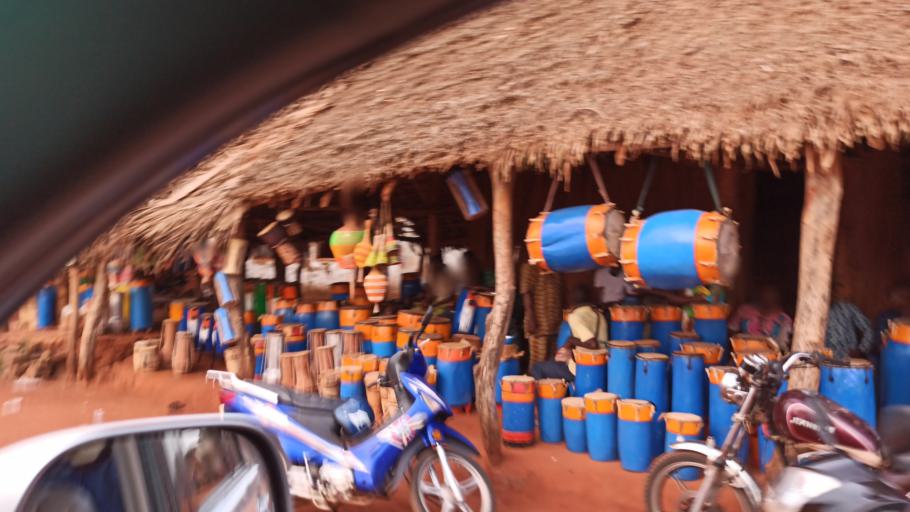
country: BJ
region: Queme
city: Porto-Novo
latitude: 6.5316
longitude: 2.6629
